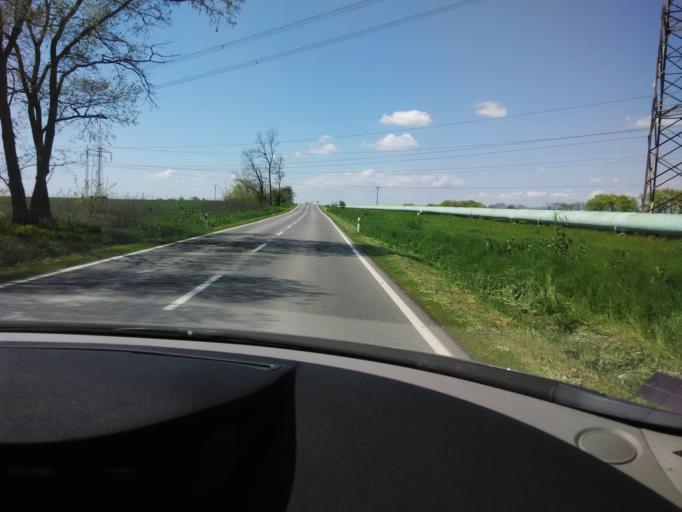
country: SK
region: Trnavsky
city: Leopoldov
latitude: 48.4441
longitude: 17.6645
